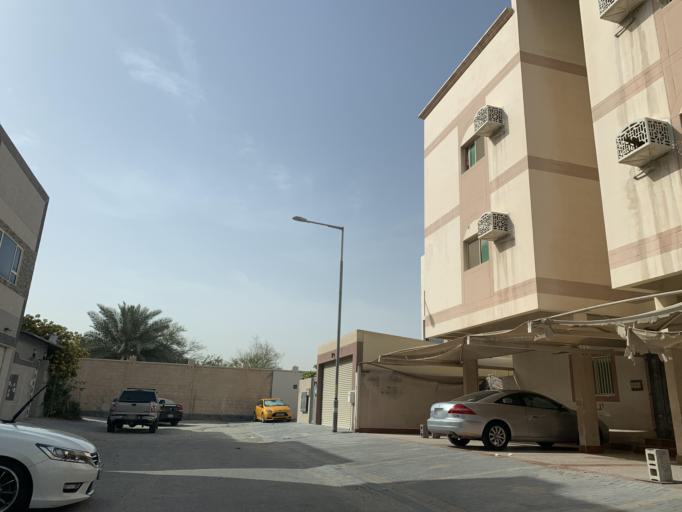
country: BH
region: Northern
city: Madinat `Isa
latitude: 26.1786
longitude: 50.5670
